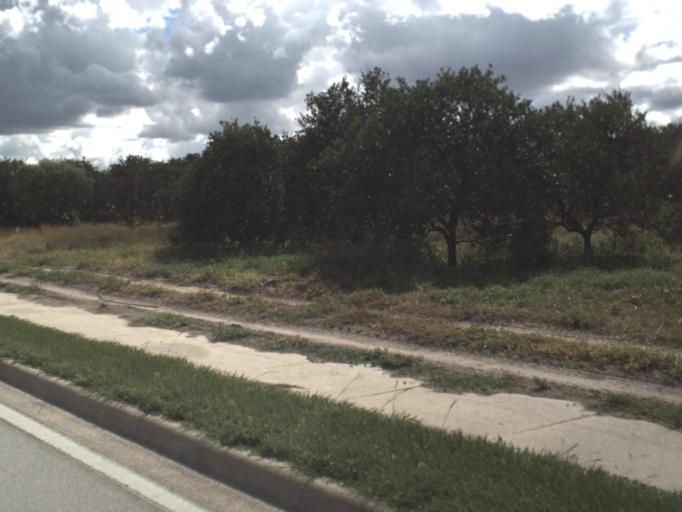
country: US
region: Florida
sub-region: Polk County
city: Eagle Lake
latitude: 27.9946
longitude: -81.7558
